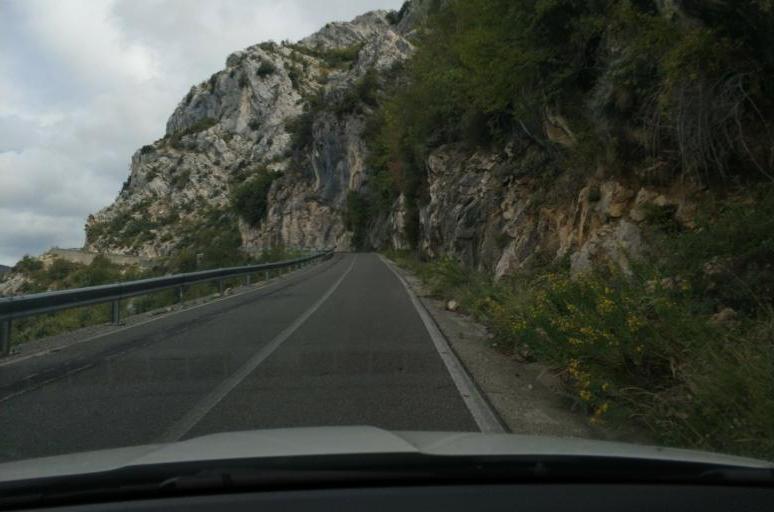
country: AL
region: Durres
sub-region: Rrethi i Krujes
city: Kruje
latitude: 41.5250
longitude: 19.7941
